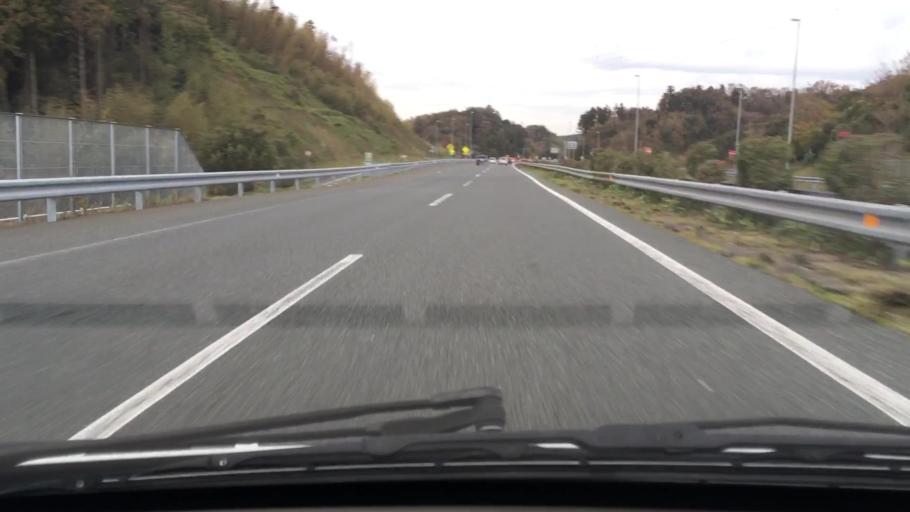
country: JP
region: Chiba
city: Kimitsu
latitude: 35.2514
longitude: 139.8919
